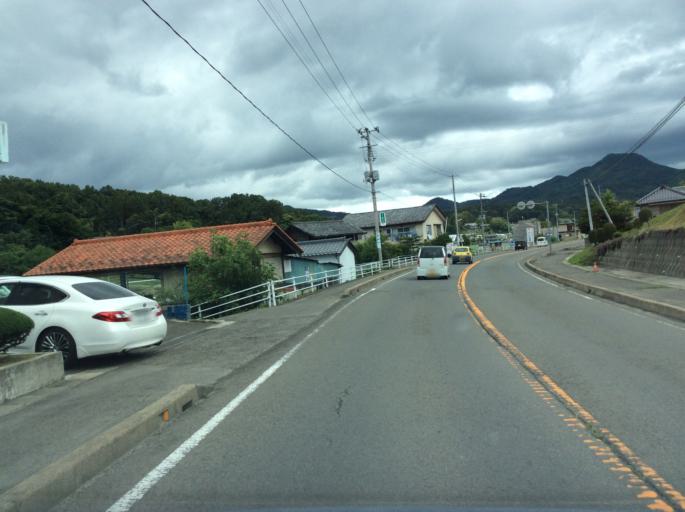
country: JP
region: Fukushima
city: Fukushima-shi
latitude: 37.6759
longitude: 140.5649
